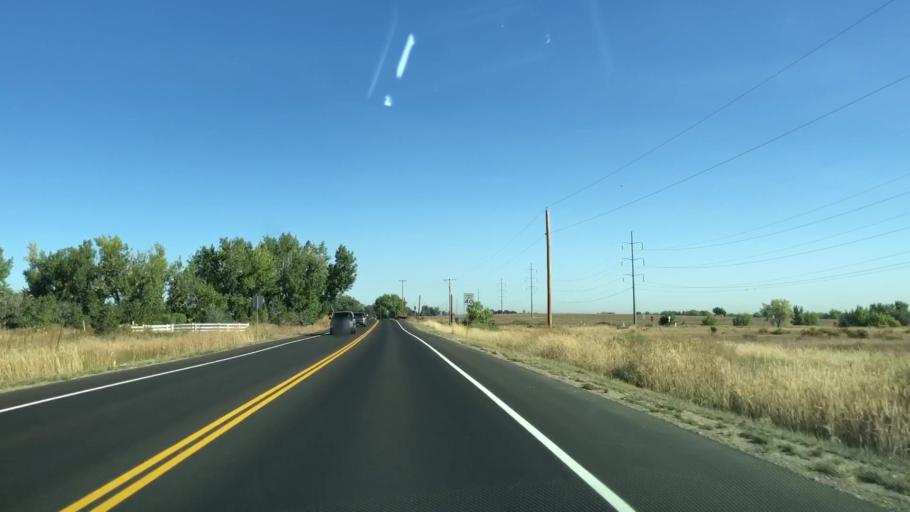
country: US
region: Colorado
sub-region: Larimer County
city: Loveland
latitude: 40.4370
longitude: -105.0454
